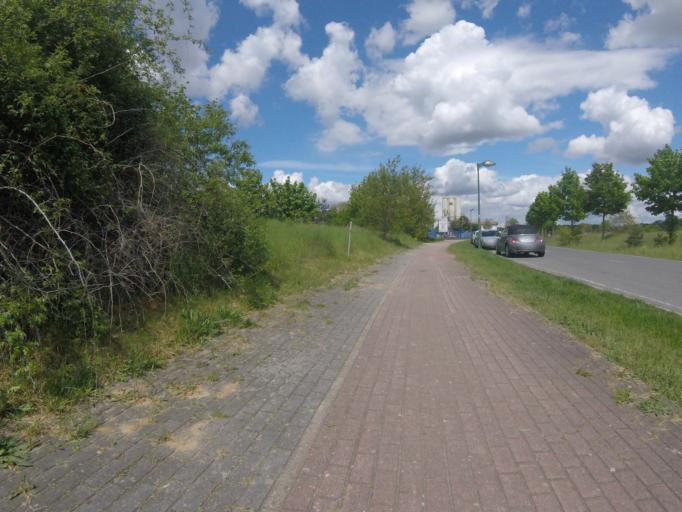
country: DE
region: Brandenburg
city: Konigs Wusterhausen
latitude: 52.3050
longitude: 13.5982
